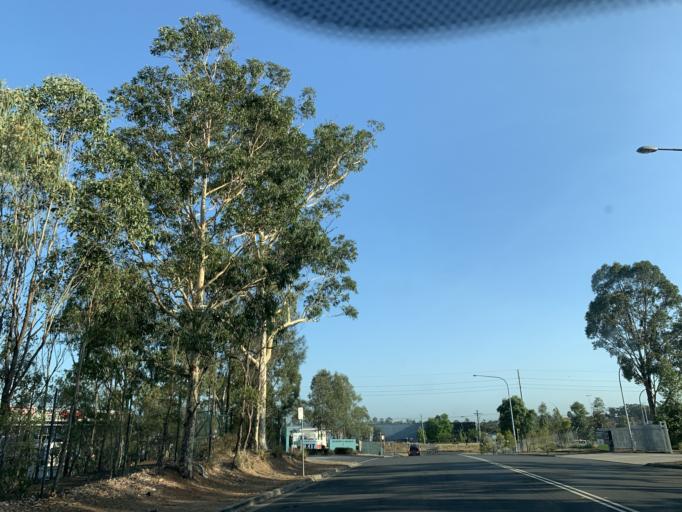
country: AU
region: New South Wales
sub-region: Blacktown
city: Doonside
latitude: -33.7971
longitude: 150.8883
